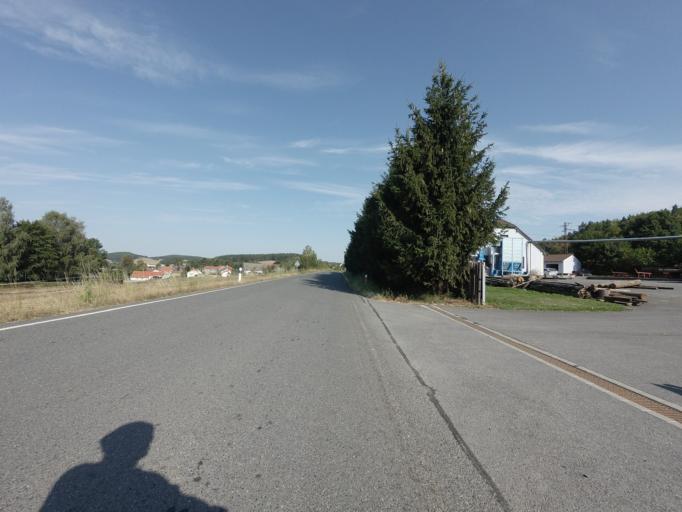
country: CZ
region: Jihocesky
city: Bernartice
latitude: 49.3246
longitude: 14.3603
